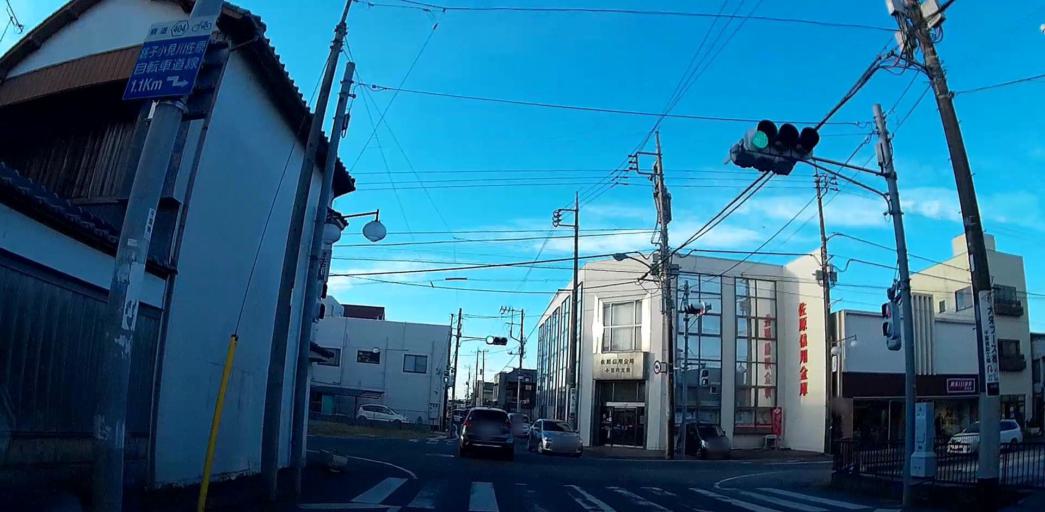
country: JP
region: Chiba
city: Omigawa
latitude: 35.8550
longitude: 140.6054
